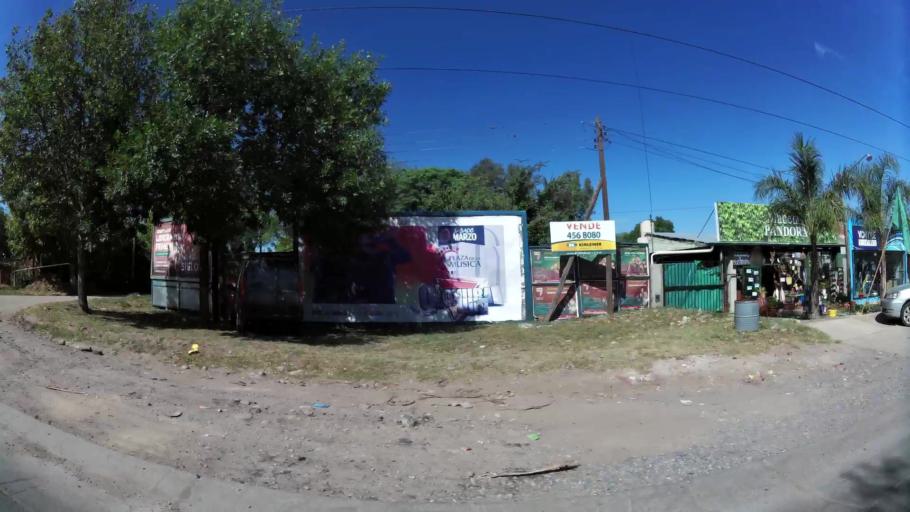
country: AR
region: Cordoba
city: Villa Allende
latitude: -31.3155
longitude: -64.2882
